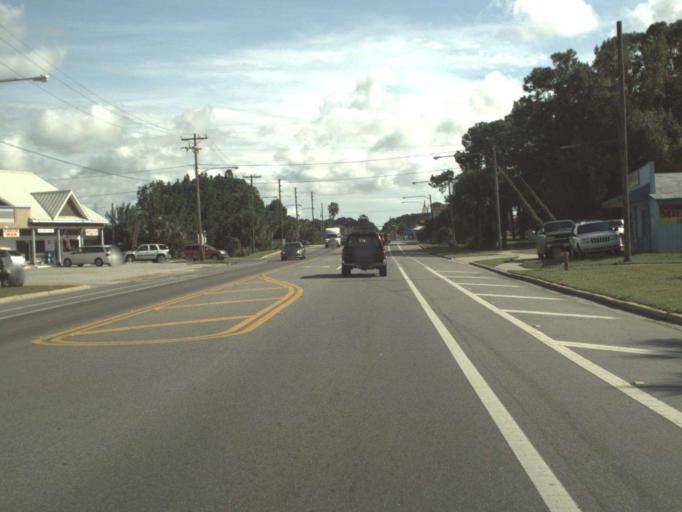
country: US
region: Florida
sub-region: Gulf County
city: Port Saint Joe
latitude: 29.8189
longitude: -85.3062
